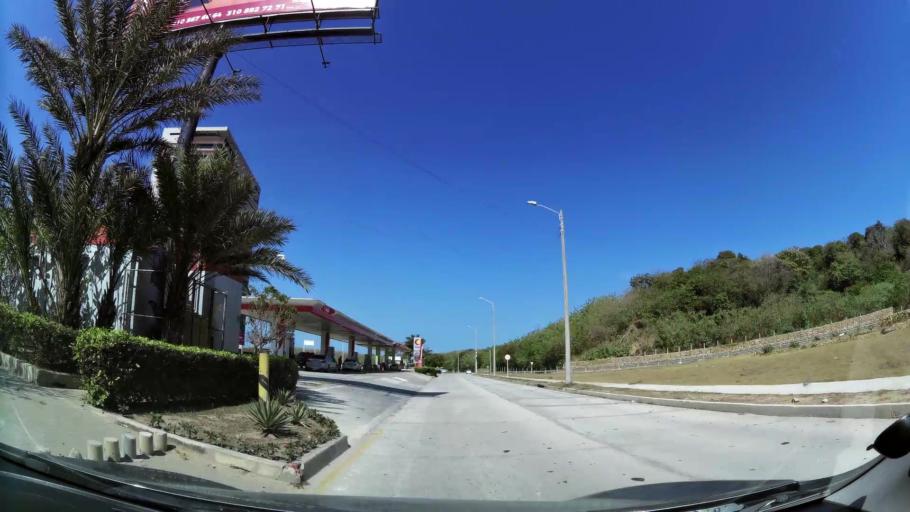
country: CO
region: Atlantico
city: Barranquilla
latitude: 11.0198
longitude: -74.8381
